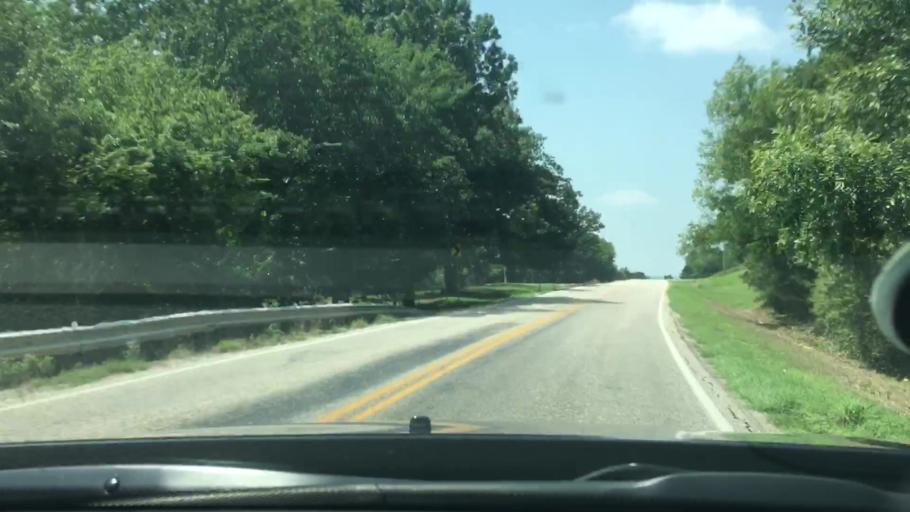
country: US
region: Oklahoma
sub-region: Johnston County
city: Tishomingo
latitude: 34.3725
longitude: -96.4590
